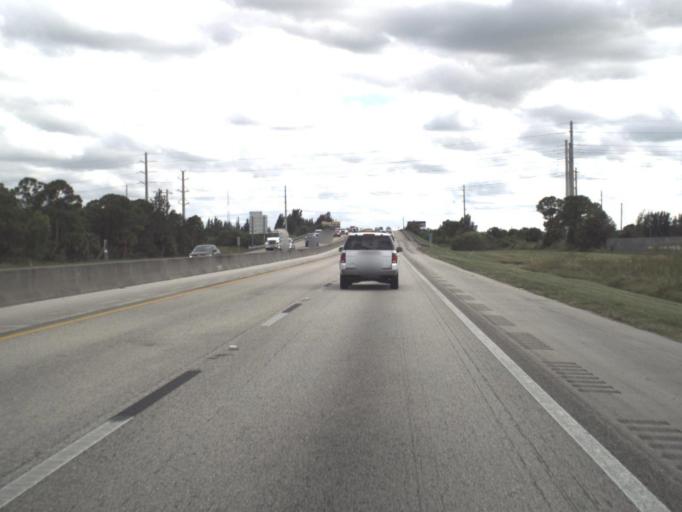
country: US
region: Florida
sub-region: Saint Lucie County
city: Fort Pierce South
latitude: 27.3843
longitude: -80.3889
